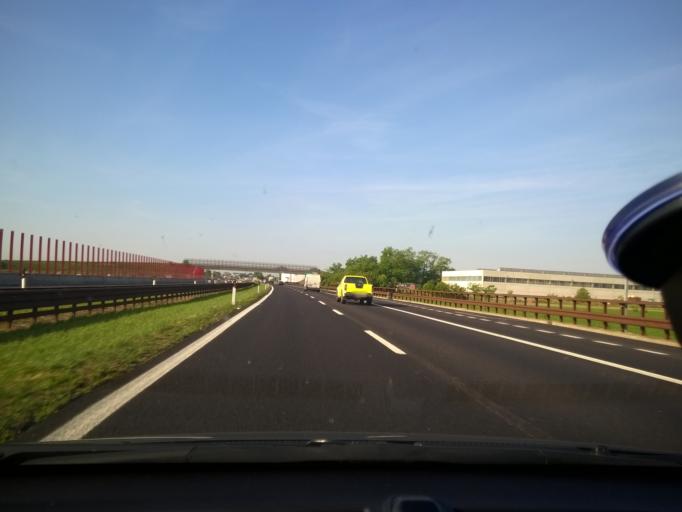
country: IT
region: Lombardy
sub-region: Provincia di Mantova
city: Bondeno
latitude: 44.9247
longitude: 10.8550
